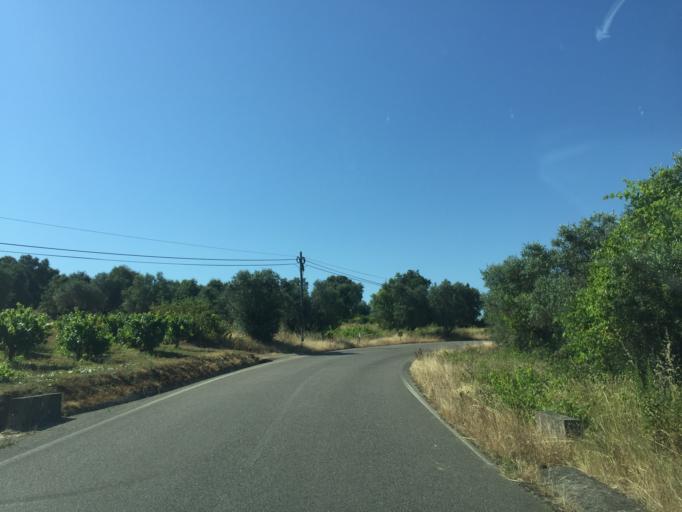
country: PT
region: Santarem
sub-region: Tomar
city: Tomar
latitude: 39.5901
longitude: -8.3277
